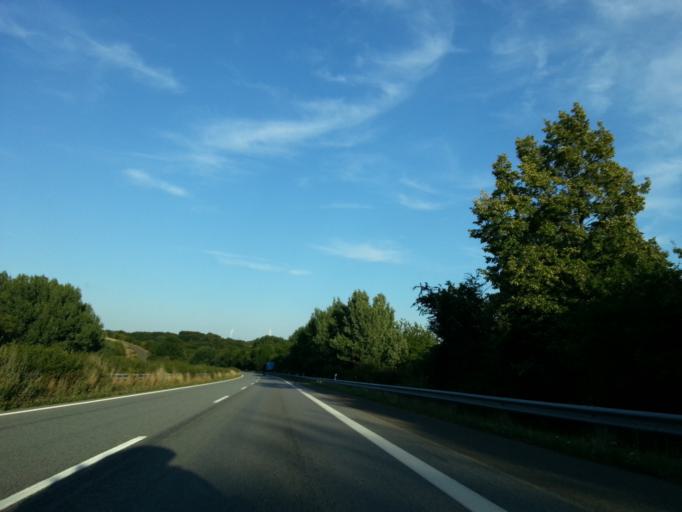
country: DE
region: Rheinland-Pfalz
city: Konken
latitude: 49.5151
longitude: 7.3505
